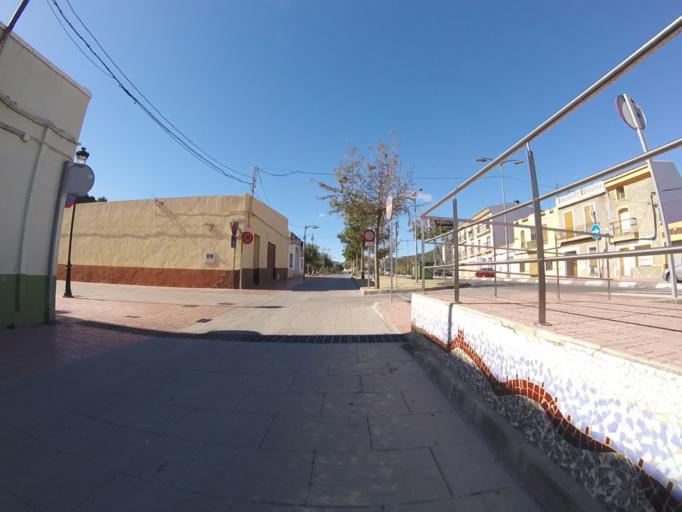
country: ES
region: Valencia
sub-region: Provincia de Castello
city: Orpesa/Oropesa del Mar
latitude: 40.0939
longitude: 0.1327
